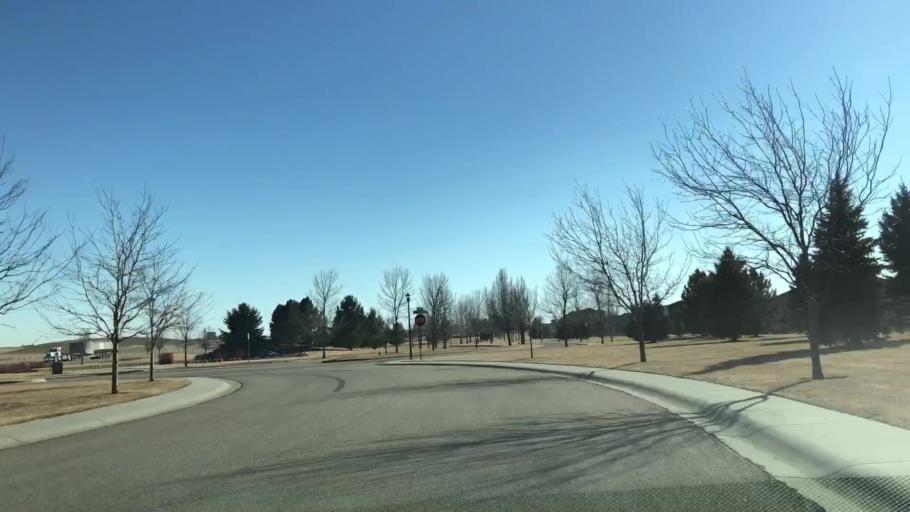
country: US
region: Colorado
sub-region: Weld County
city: Windsor
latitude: 40.4550
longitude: -104.9453
